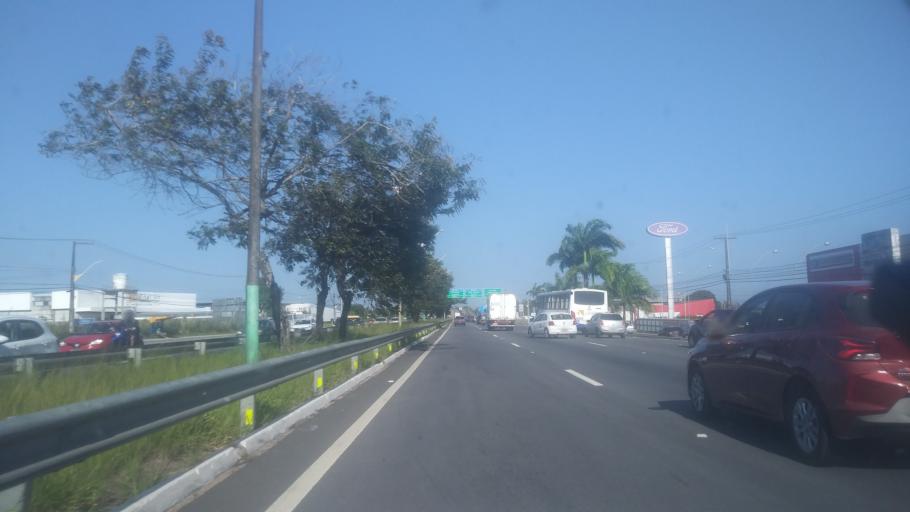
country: BR
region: Rio Grande do Norte
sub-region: Parnamirim
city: Parnamirim
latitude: -5.8905
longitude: -35.2503
